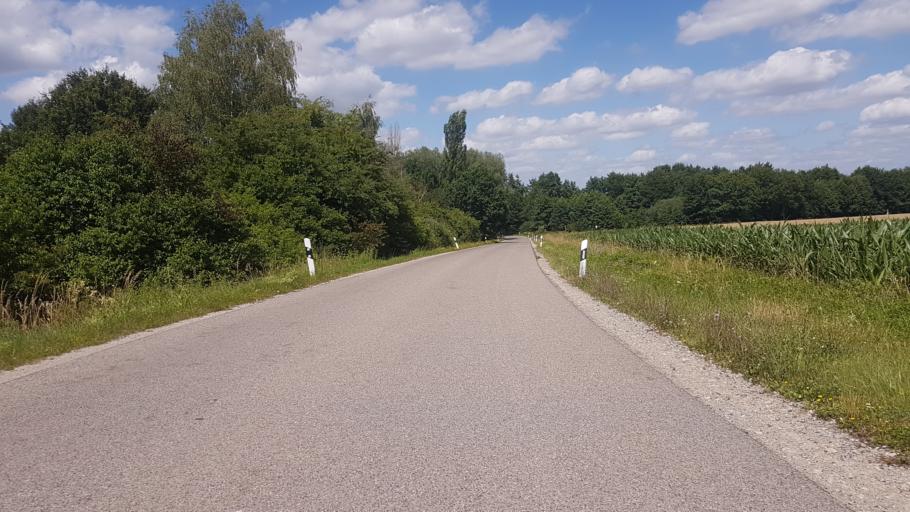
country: DE
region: Bavaria
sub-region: Regierungsbezirk Mittelfranken
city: Geslau
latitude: 49.3402
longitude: 10.3327
